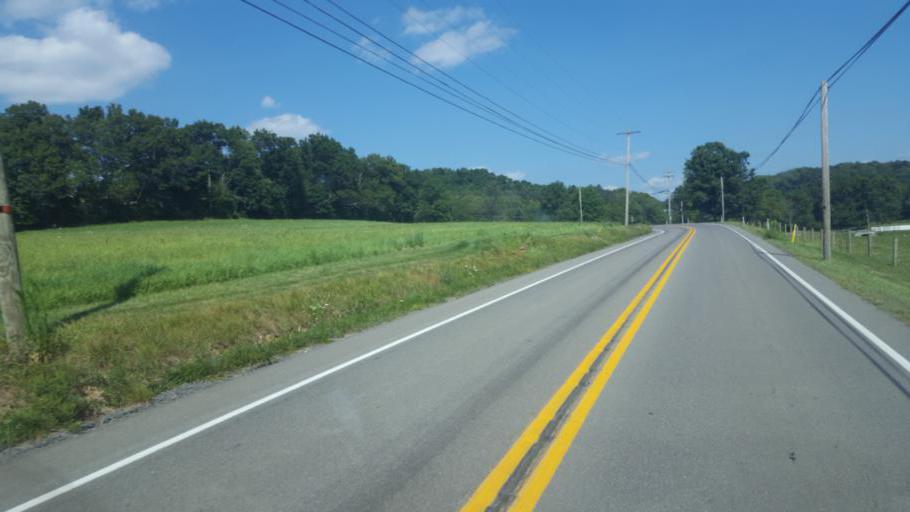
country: US
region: Pennsylvania
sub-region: Clarion County
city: Clarion
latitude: 41.1210
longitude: -79.4351
